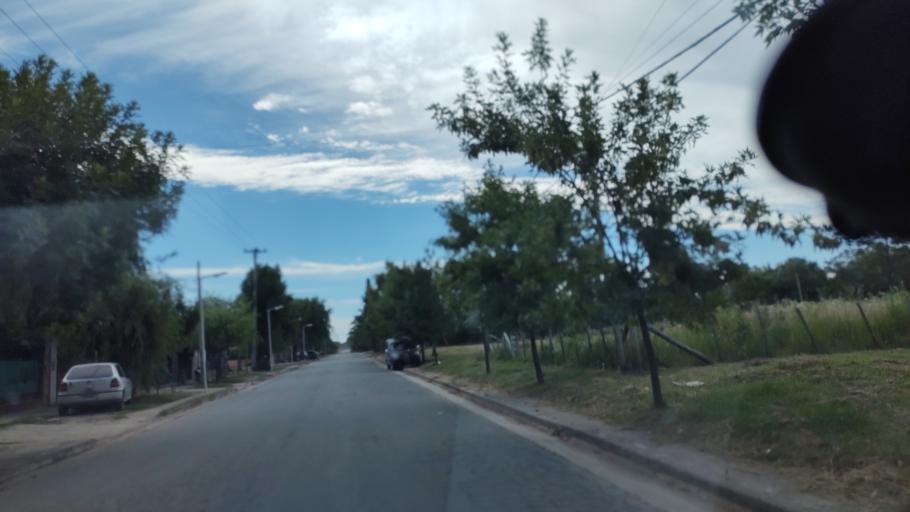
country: AR
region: Buenos Aires
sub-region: Partido de Lobos
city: Lobos
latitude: -35.1776
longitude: -59.1065
